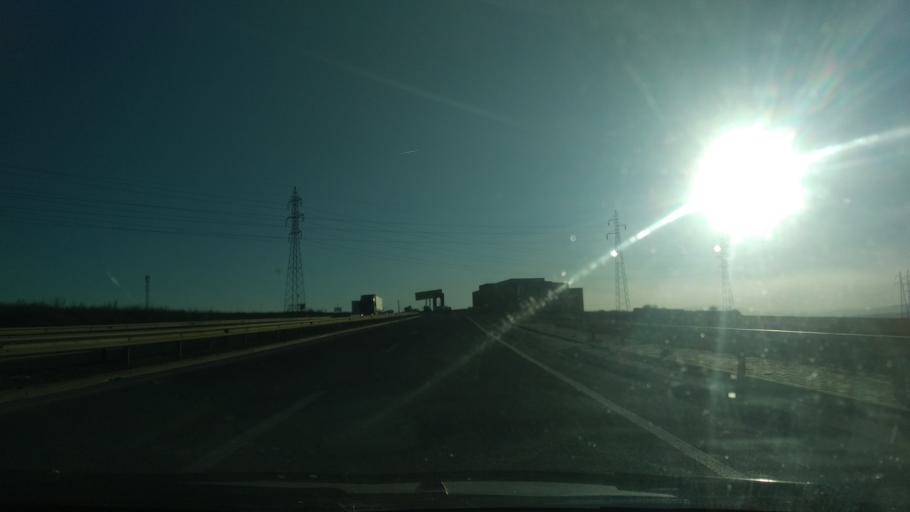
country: XK
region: Pristina
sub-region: Kosovo Polje
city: Kosovo Polje
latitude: 42.6818
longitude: 21.1168
